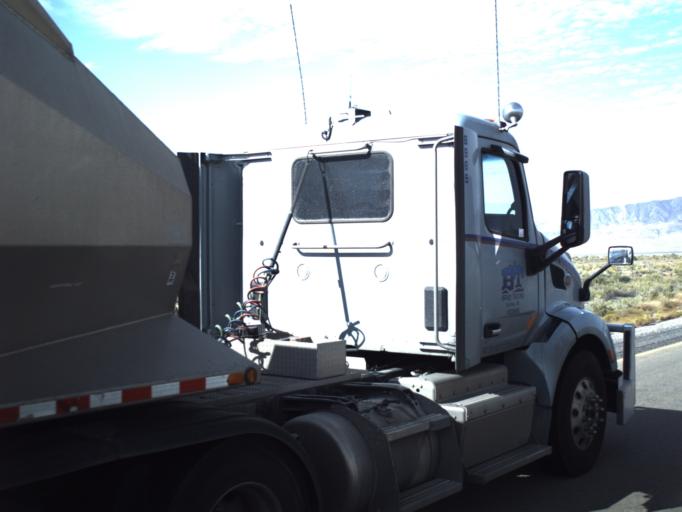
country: US
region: Utah
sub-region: Tooele County
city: Grantsville
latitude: 40.7552
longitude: -112.7440
